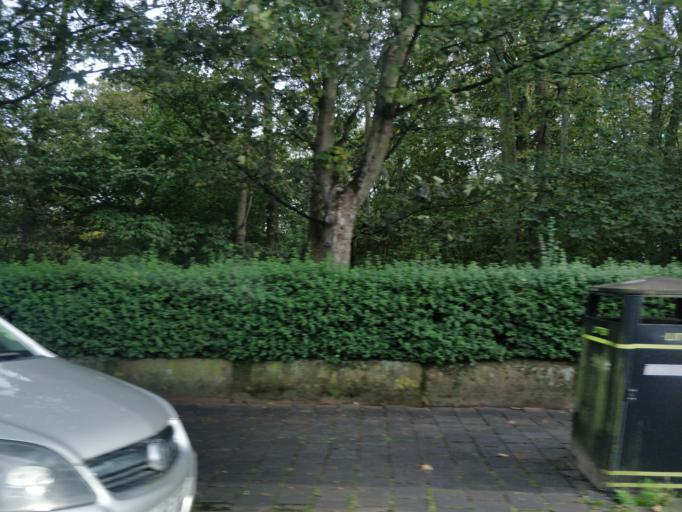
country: GB
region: England
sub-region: Sefton
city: Southport
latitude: 53.6577
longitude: -2.9884
